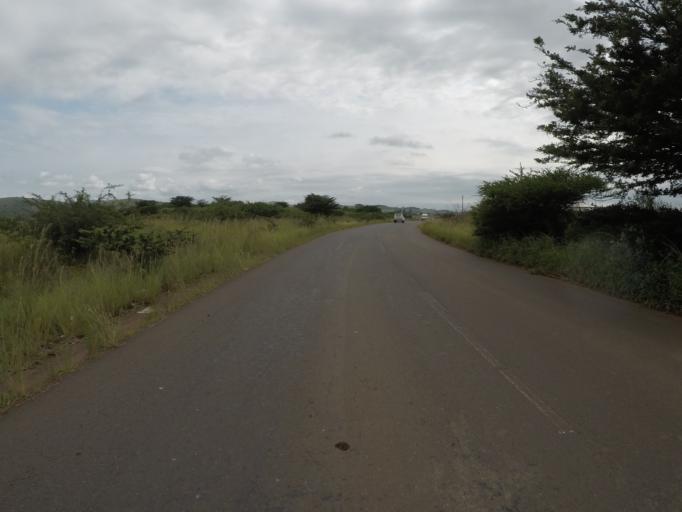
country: ZA
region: KwaZulu-Natal
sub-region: uThungulu District Municipality
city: Empangeni
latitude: -28.7219
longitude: 31.8673
